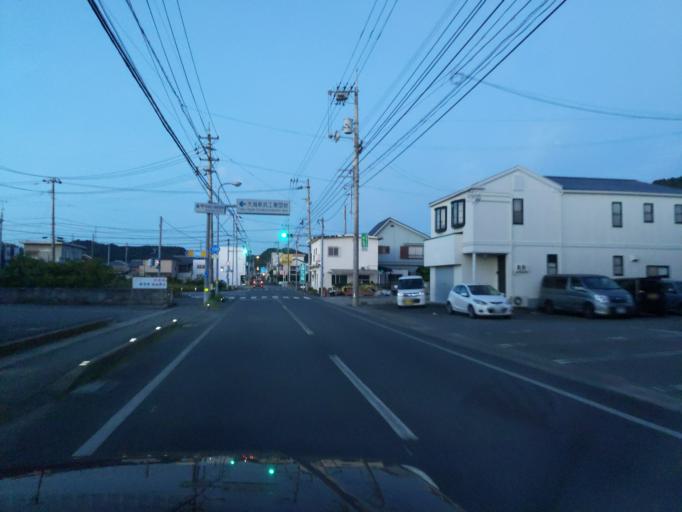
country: JP
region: Tokushima
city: Anan
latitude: 33.8916
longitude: 134.6574
